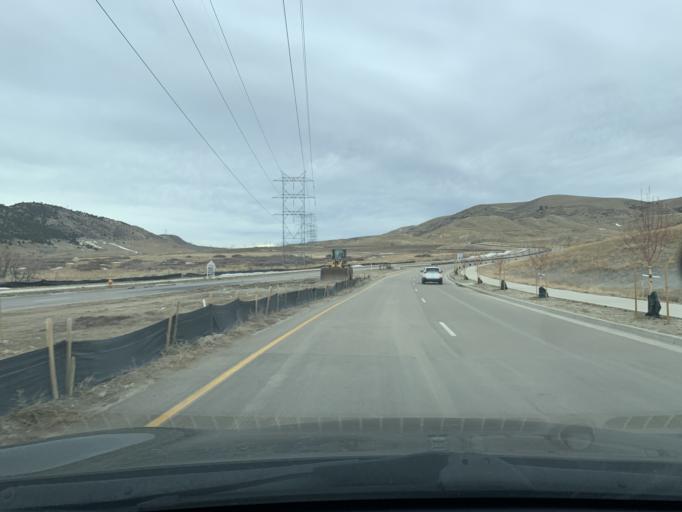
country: US
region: Colorado
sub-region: Jefferson County
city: West Pleasant View
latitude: 39.6784
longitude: -105.1838
